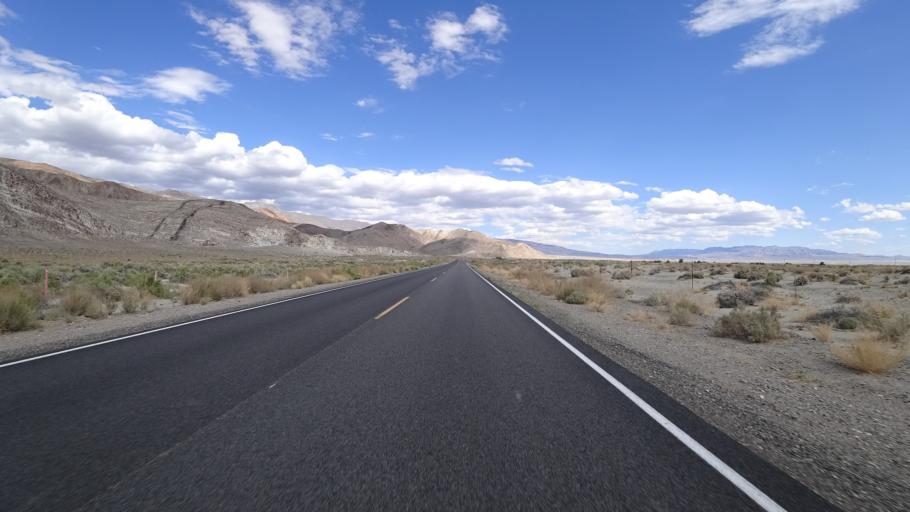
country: US
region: California
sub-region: Inyo County
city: Lone Pine
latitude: 36.5311
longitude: -117.9154
